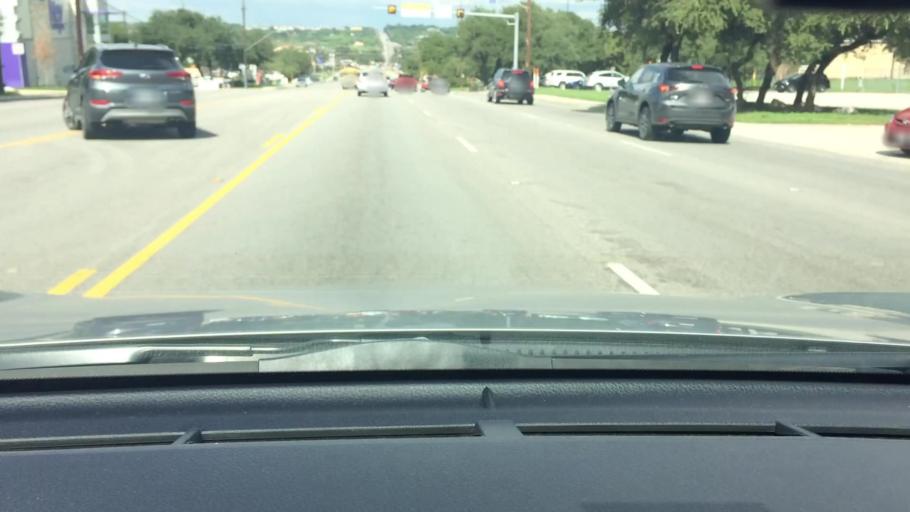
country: US
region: Texas
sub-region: Bexar County
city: Shavano Park
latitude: 29.5500
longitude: -98.5733
